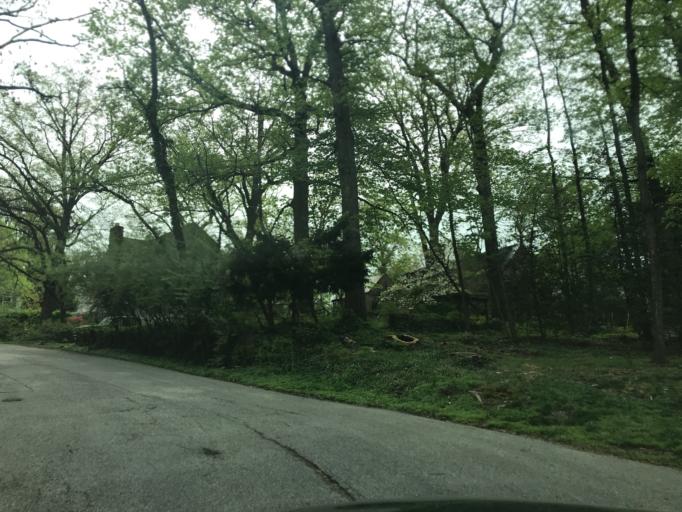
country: US
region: Maryland
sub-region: Baltimore County
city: Catonsville
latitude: 39.2629
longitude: -76.7486
